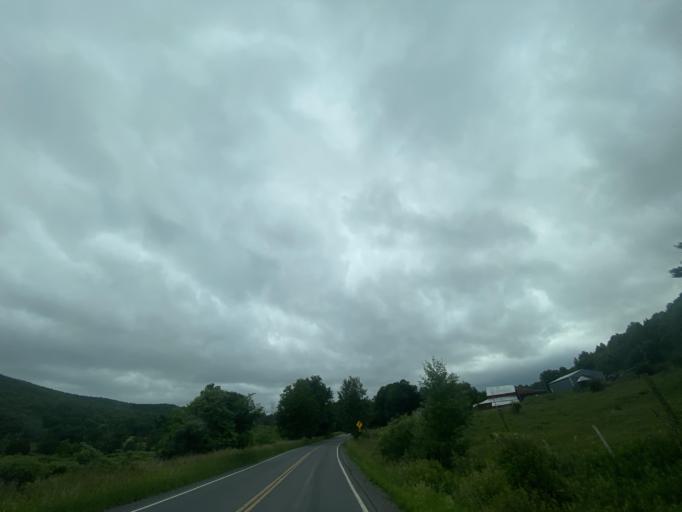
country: US
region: New York
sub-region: Schoharie County
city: Middleburgh
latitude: 42.3857
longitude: -74.3560
